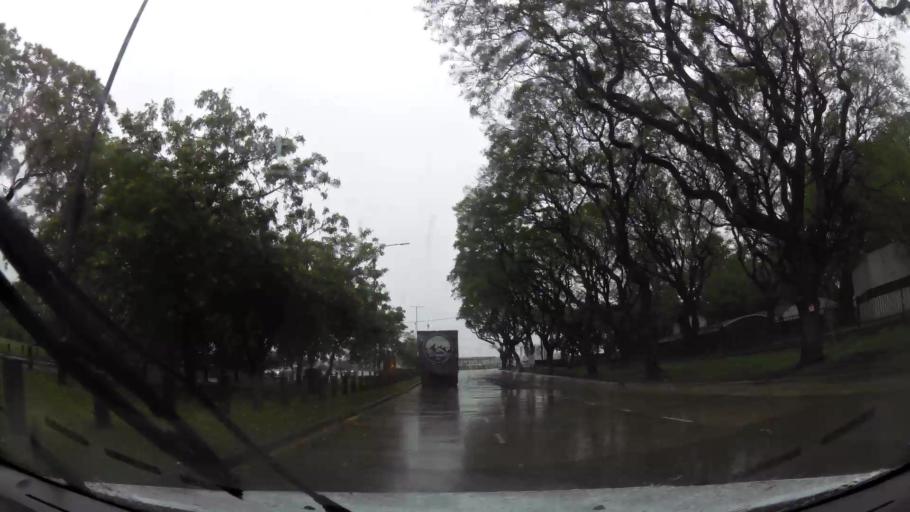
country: AR
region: Buenos Aires F.D.
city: Colegiales
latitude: -34.5633
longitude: -58.4175
